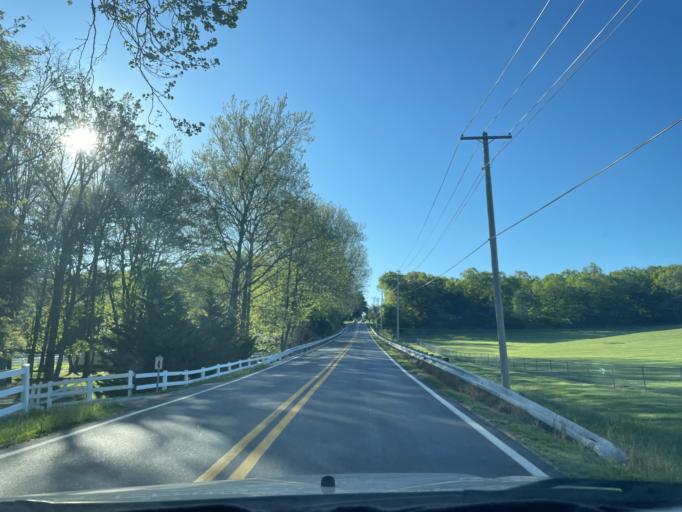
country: US
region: Maryland
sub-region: Carroll County
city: Mount Airy
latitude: 39.4108
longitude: -77.1329
